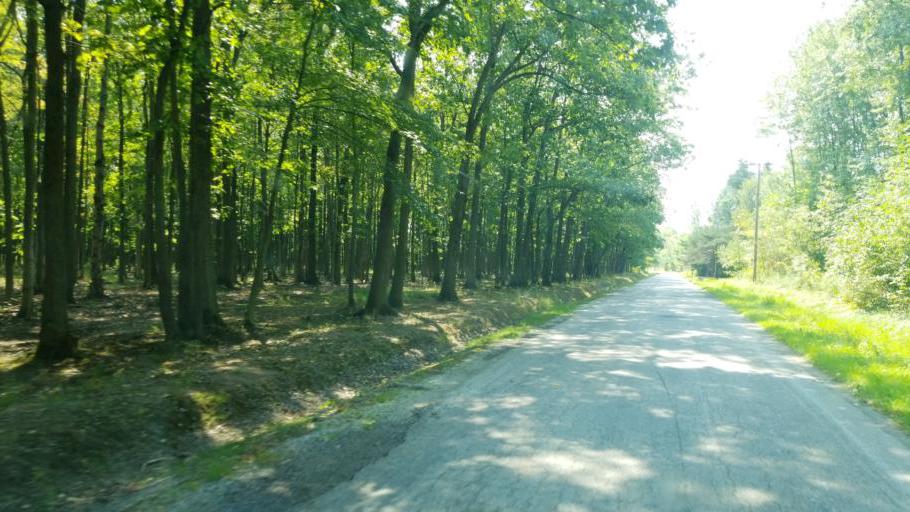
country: US
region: Ohio
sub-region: Ashtabula County
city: Orwell
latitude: 41.5756
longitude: -80.9923
